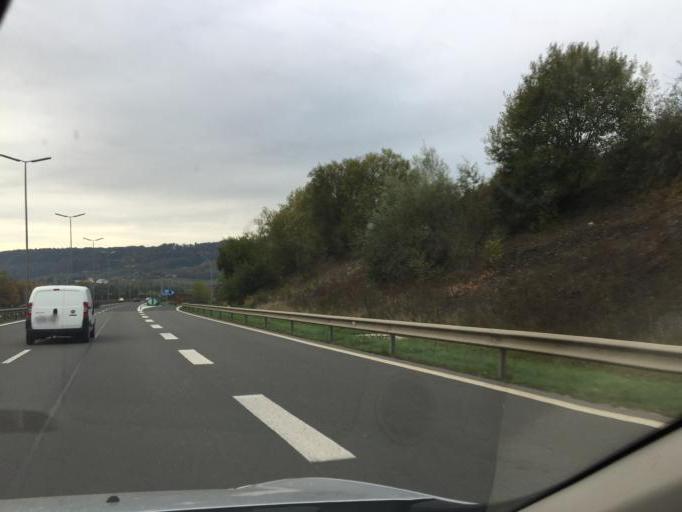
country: LU
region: Luxembourg
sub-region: Canton de Mersch
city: Mersch
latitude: 49.7563
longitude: 6.0918
